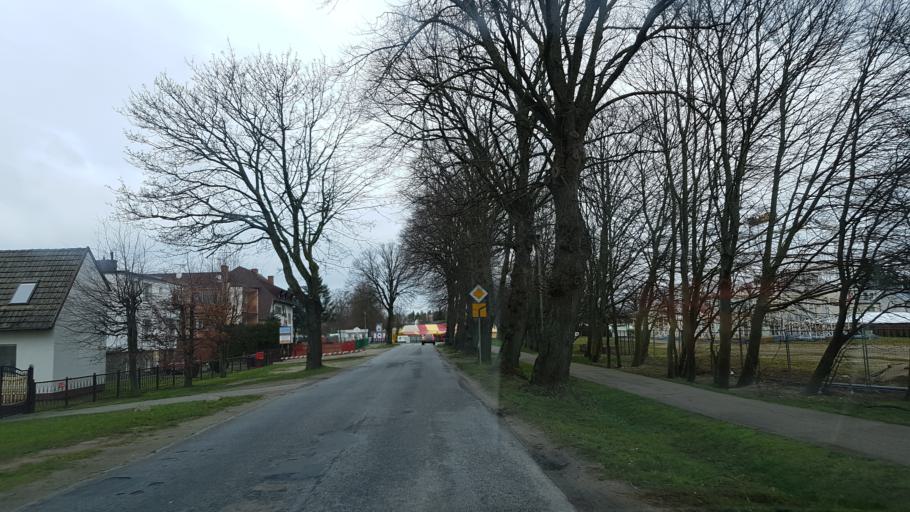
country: PL
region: West Pomeranian Voivodeship
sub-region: Powiat kolobrzeski
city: Ustronie Morskie
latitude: 54.2105
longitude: 15.7461
